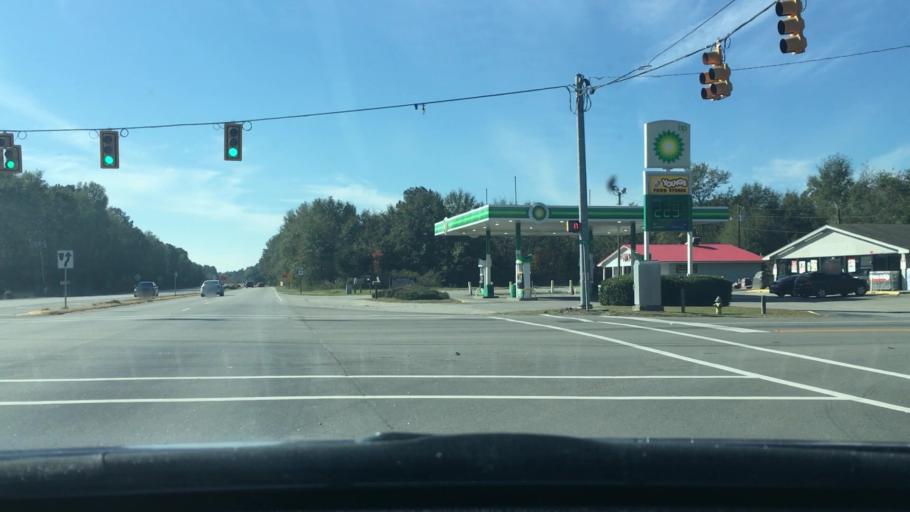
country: US
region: South Carolina
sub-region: Sumter County
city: Lakewood
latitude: 33.8676
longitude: -80.3583
